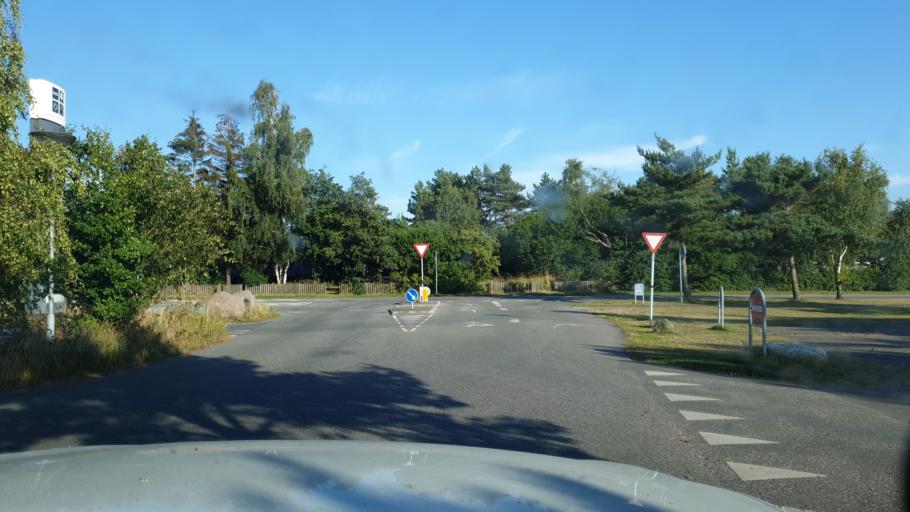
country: DK
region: Zealand
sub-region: Guldborgsund Kommune
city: Nykobing Falster
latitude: 54.6979
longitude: 11.9580
